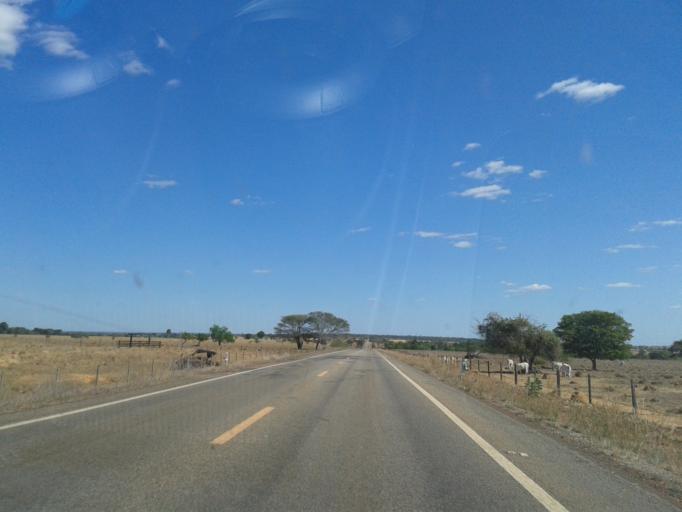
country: BR
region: Goias
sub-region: Sao Miguel Do Araguaia
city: Sao Miguel do Araguaia
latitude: -13.4324
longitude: -50.2823
